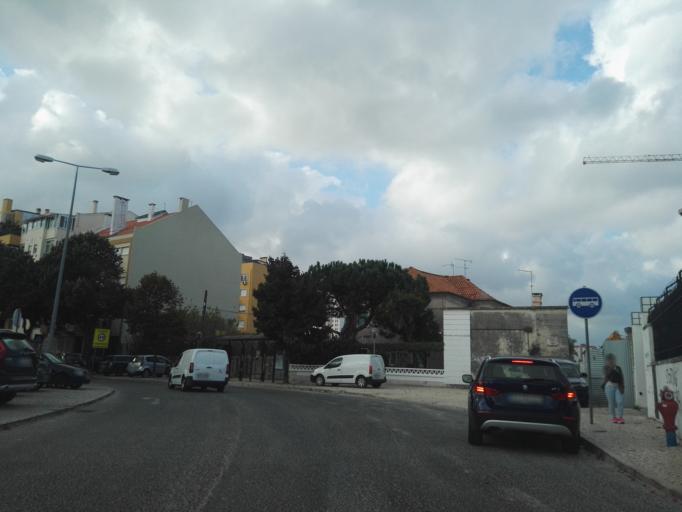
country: PT
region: Lisbon
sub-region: Odivelas
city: Olival do Basto
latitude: 38.7742
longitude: -9.1565
